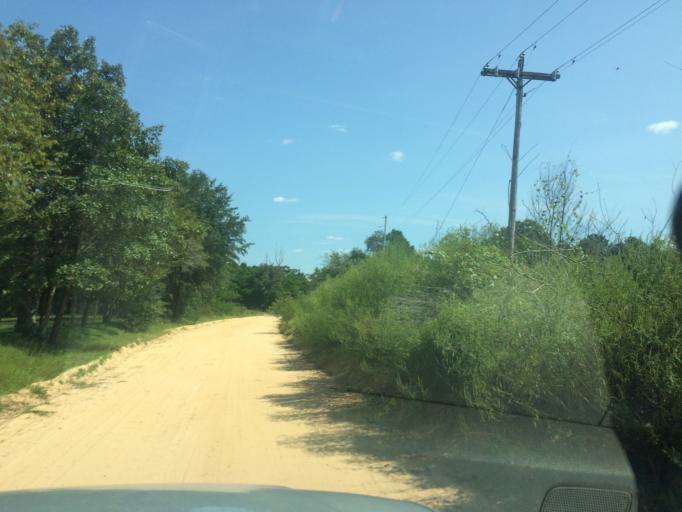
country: US
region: South Carolina
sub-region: Barnwell County
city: Williston
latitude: 33.6040
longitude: -81.4804
